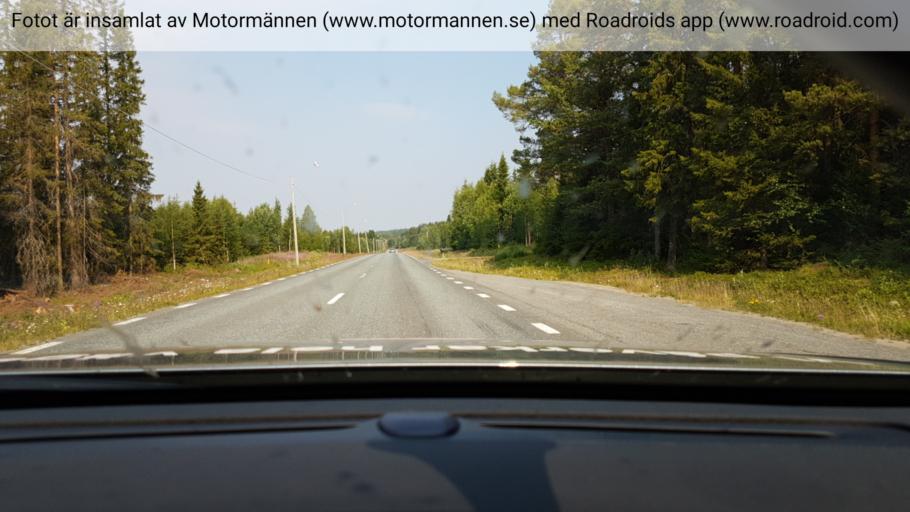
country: SE
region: Vaesterbotten
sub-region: Vilhelmina Kommun
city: Sjoberg
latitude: 65.4620
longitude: 16.0822
